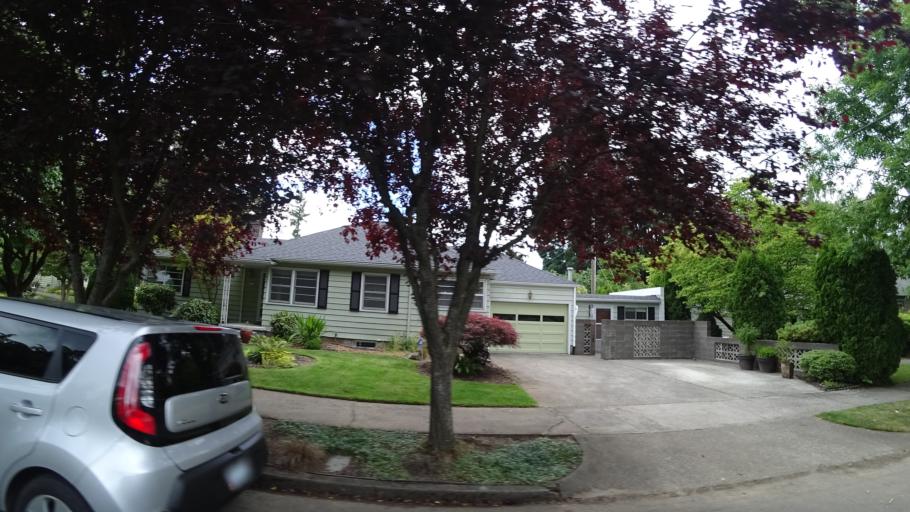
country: US
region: Oregon
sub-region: Multnomah County
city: Portland
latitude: 45.5755
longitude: -122.7176
